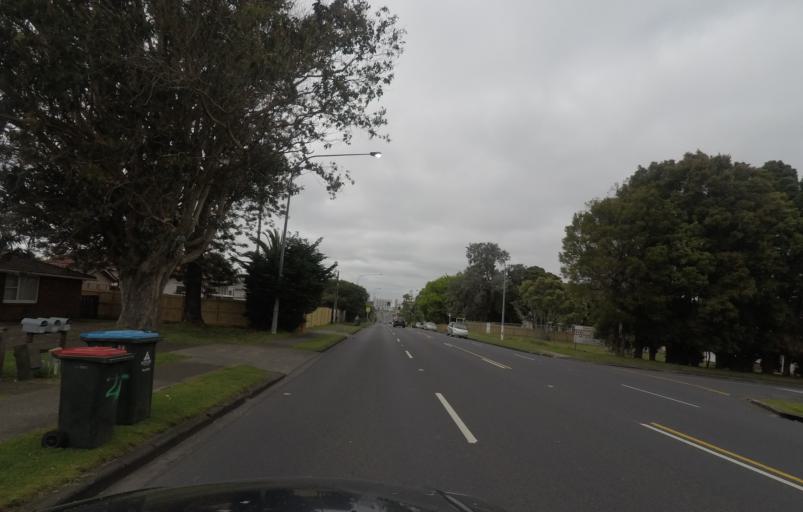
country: NZ
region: Auckland
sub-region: Auckland
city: Wiri
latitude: -36.9531
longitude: 174.8466
